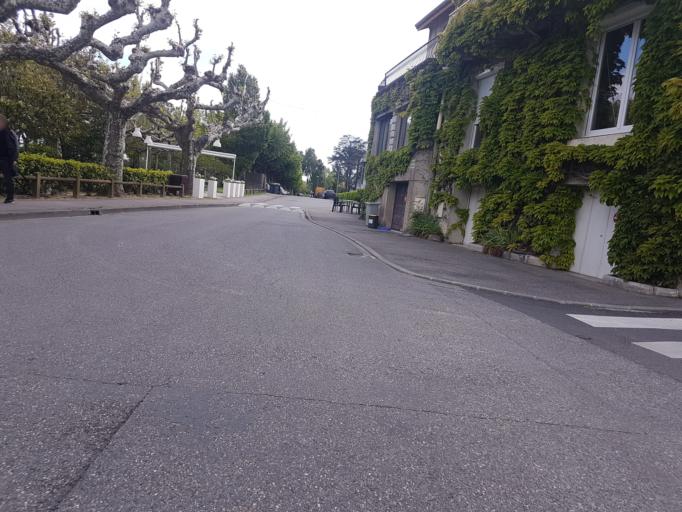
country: FR
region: Rhone-Alpes
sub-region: Departement de l'Ardeche
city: Guilherand-Granges
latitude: 44.9312
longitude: 4.8797
